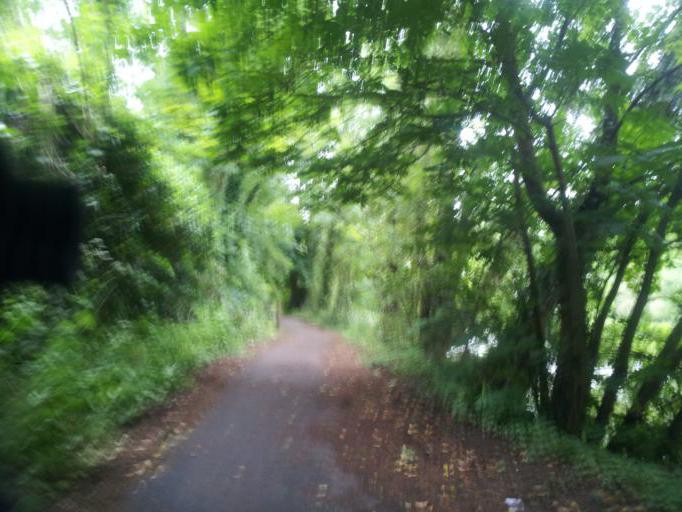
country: GB
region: England
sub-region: Kent
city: Maidstone
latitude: 51.2812
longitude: 0.5153
